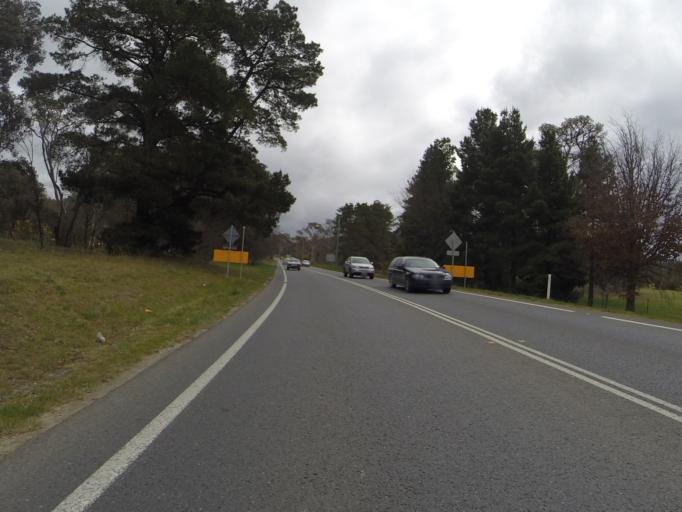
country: AU
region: Australian Capital Territory
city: Canberra
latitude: -35.2900
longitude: 149.1694
